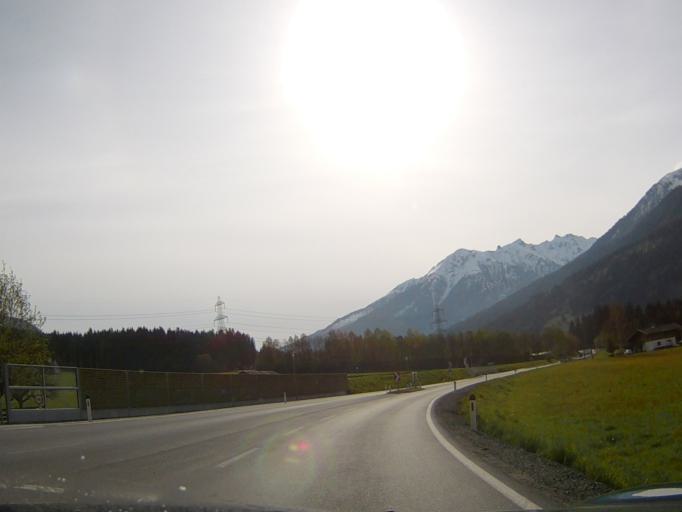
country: AT
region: Salzburg
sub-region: Politischer Bezirk Zell am See
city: Neukirchen am Grossvenediger
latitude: 47.2476
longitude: 12.2547
